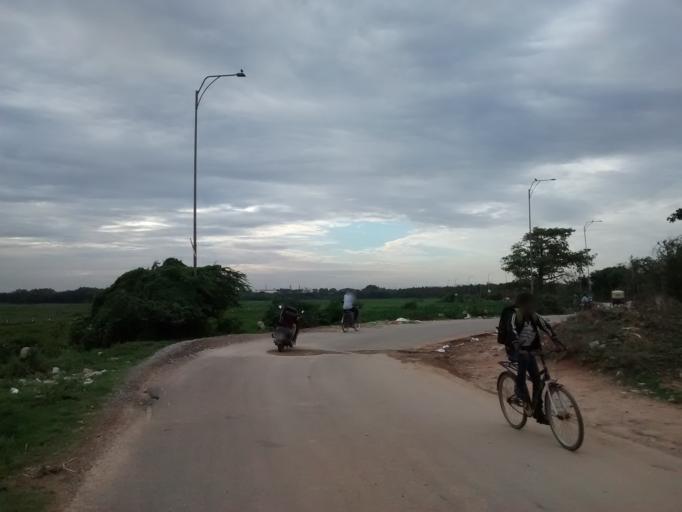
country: IN
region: Karnataka
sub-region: Bangalore Urban
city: Bangalore
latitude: 12.9325
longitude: 77.6769
